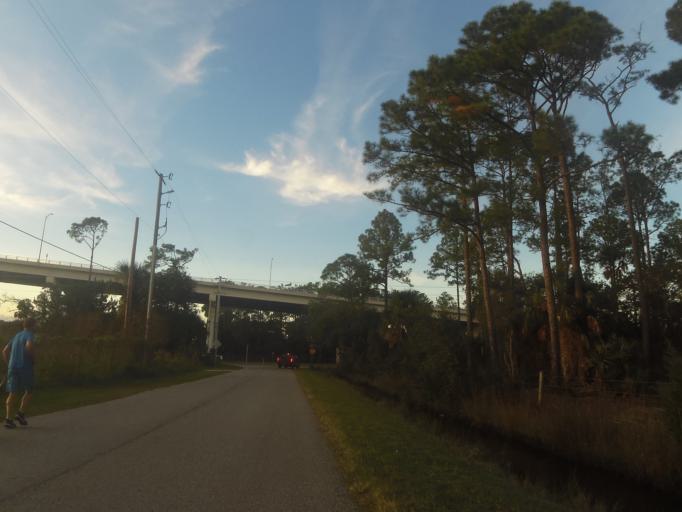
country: US
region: Florida
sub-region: Saint Johns County
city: Palm Valley
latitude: 30.1328
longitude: -81.3832
